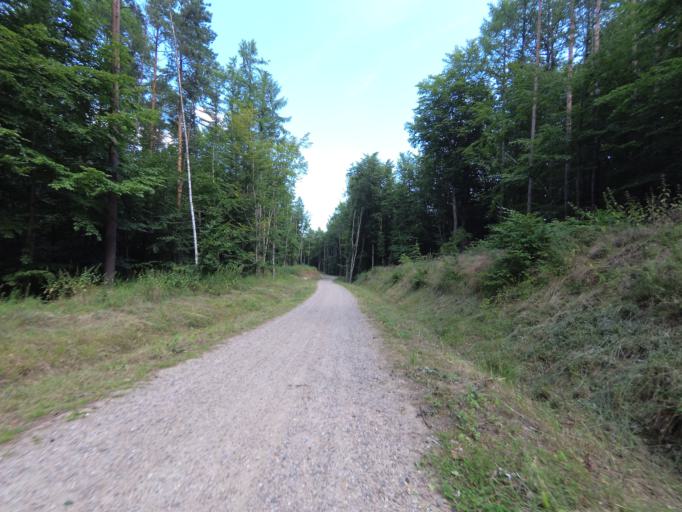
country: PL
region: Pomeranian Voivodeship
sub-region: Gdynia
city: Wielki Kack
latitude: 54.4821
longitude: 18.5016
